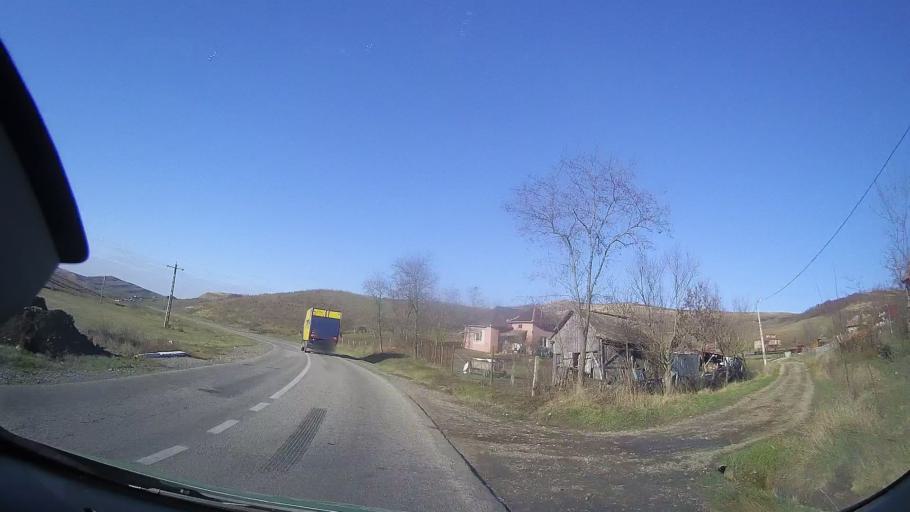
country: RO
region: Cluj
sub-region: Comuna Camarasu
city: Camarasu
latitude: 46.8009
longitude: 24.1635
